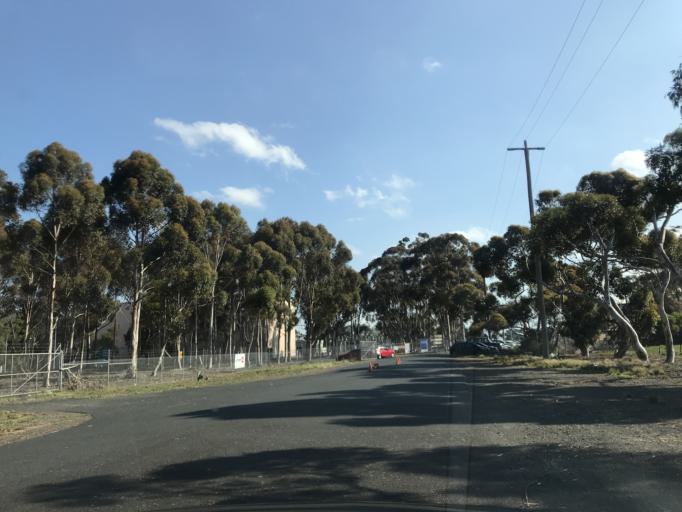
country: AU
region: Victoria
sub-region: Wyndham
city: Hoppers Crossing
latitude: -37.8878
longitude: 144.7049
